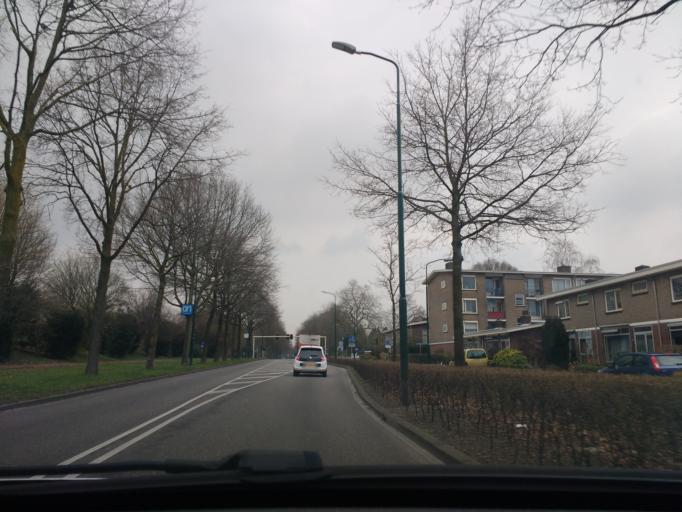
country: NL
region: Utrecht
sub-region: Gemeente Veenendaal
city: Veenendaal
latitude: 52.0333
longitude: 5.5442
